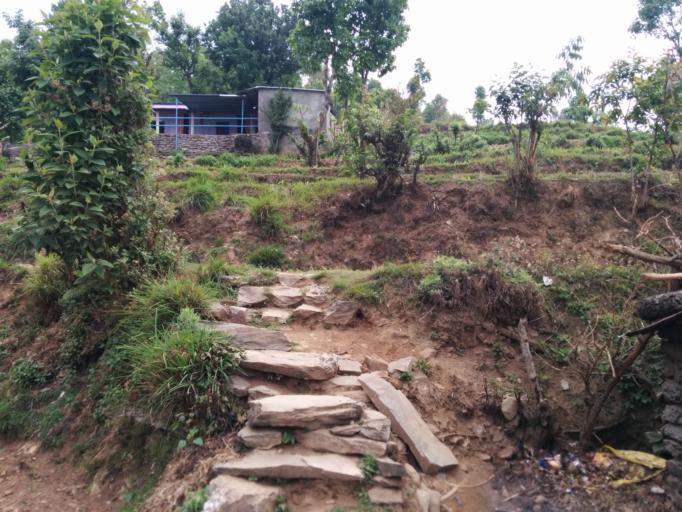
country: NP
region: Western Region
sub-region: Gandaki Zone
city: Pokhara
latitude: 28.2401
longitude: 83.9501
